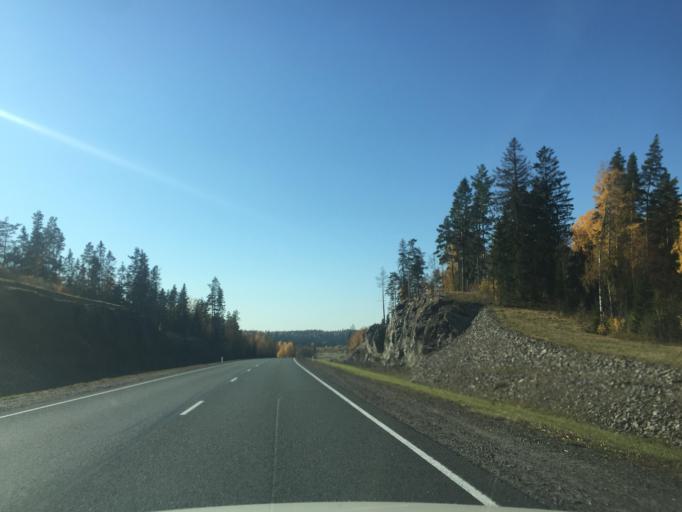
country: RU
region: Leningrad
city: Kuznechnoye
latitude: 61.3447
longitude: 29.8727
